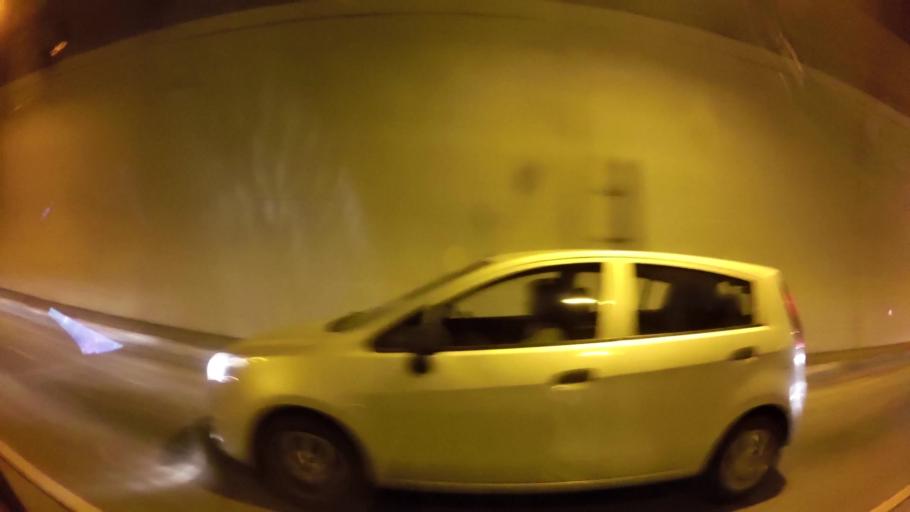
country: EC
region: Guayas
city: Eloy Alfaro
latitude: -2.1812
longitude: -79.8808
